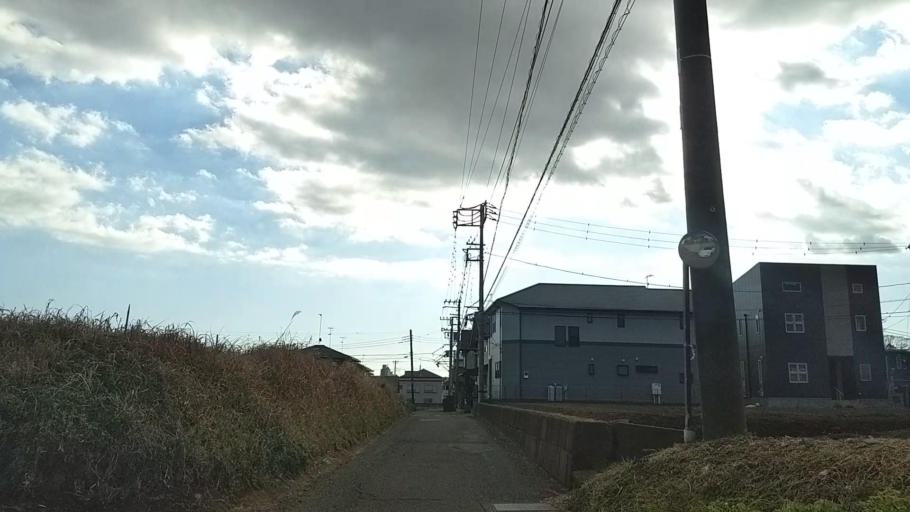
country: JP
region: Kanagawa
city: Isehara
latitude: 35.4073
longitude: 139.3109
